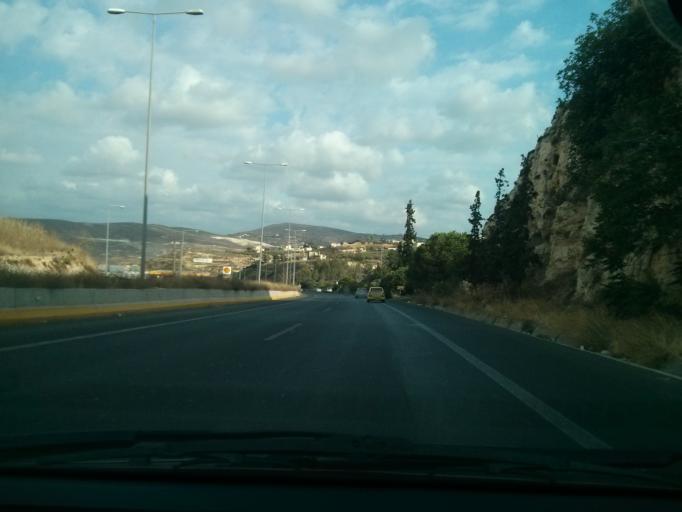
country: GR
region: Crete
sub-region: Nomos Irakleiou
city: Nea Alikarnassos
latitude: 35.3234
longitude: 25.1820
